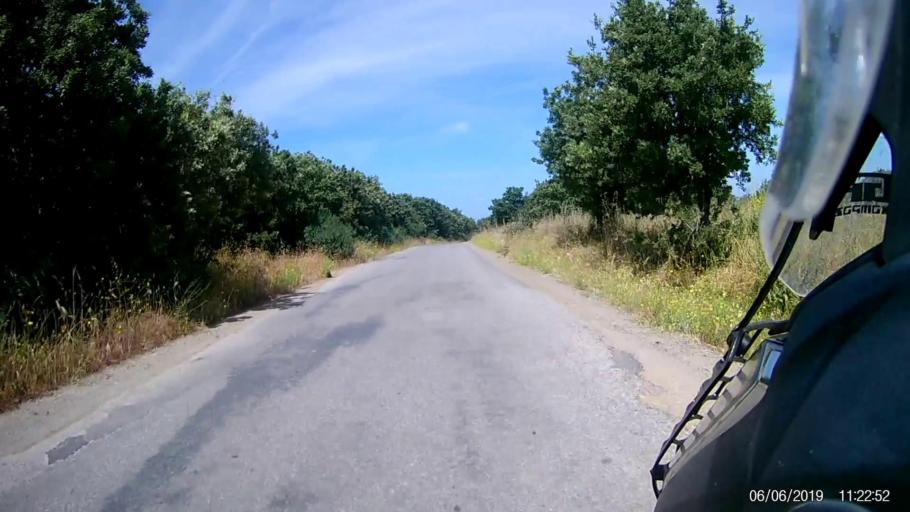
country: TR
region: Canakkale
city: Gulpinar
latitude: 39.6123
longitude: 26.1827
